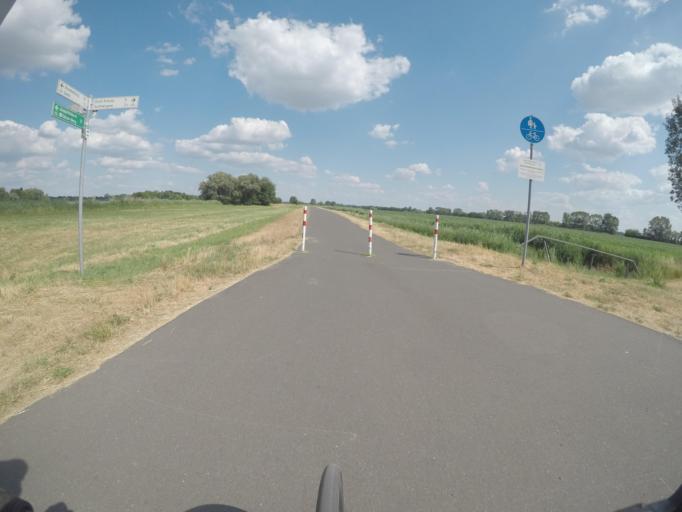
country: DE
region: Brandenburg
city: Ketzin
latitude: 52.4615
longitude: 12.8534
